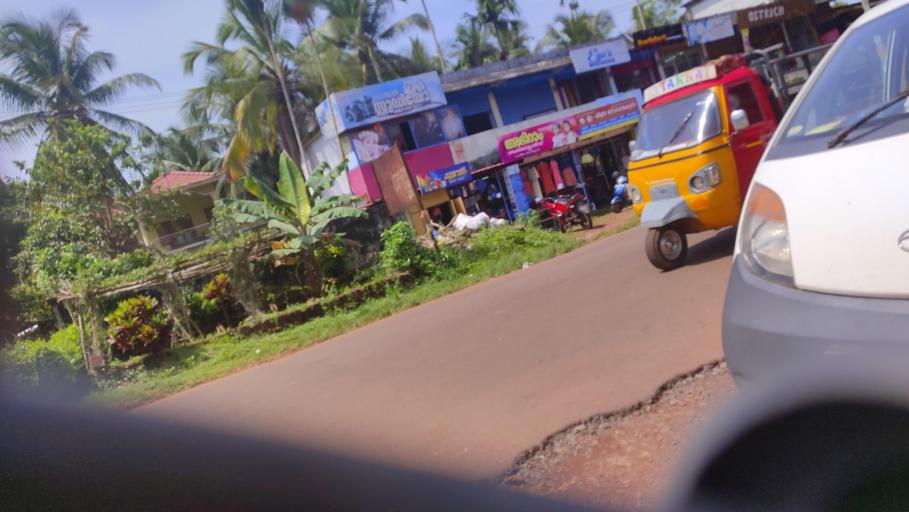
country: IN
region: Kerala
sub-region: Kasaragod District
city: Kannangad
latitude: 12.4021
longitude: 75.0983
